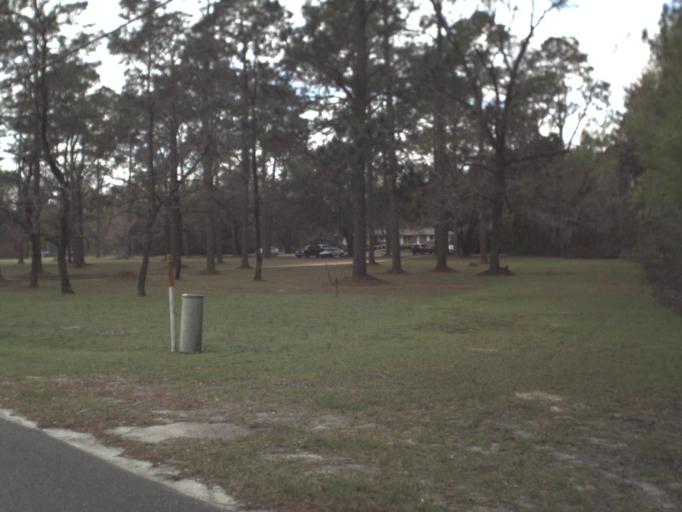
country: US
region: Florida
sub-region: Wakulla County
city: Crawfordville
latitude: 30.1687
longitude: -84.3770
